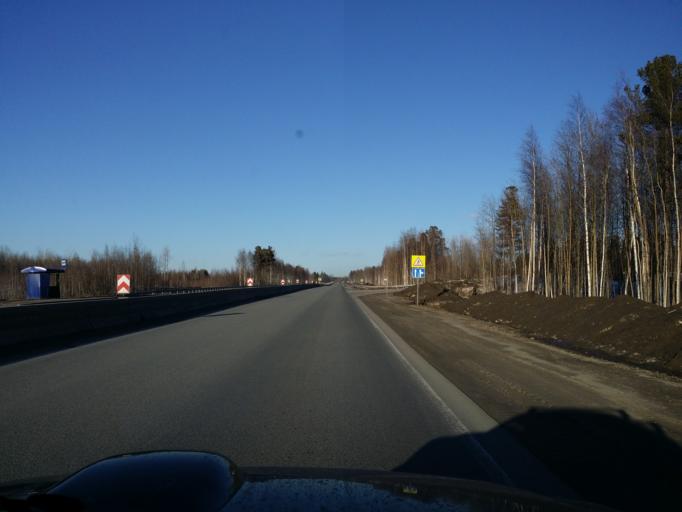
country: RU
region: Khanty-Mansiyskiy Avtonomnyy Okrug
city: Megion
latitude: 61.0595
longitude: 76.1653
